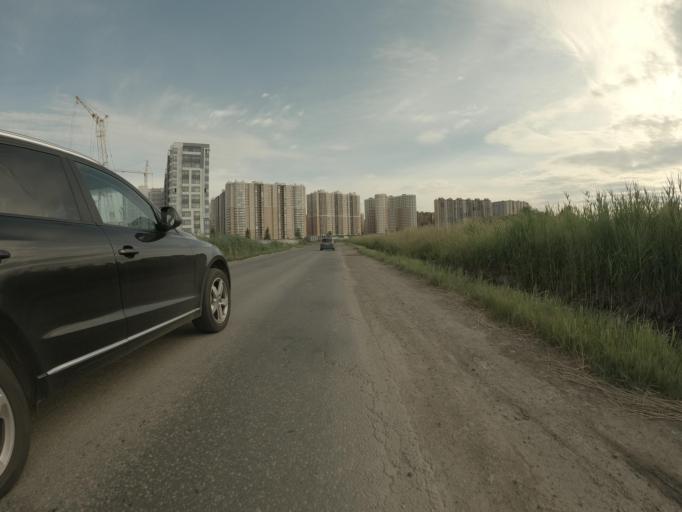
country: RU
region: St.-Petersburg
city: Krasnogvargeisky
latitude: 59.9227
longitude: 30.5170
